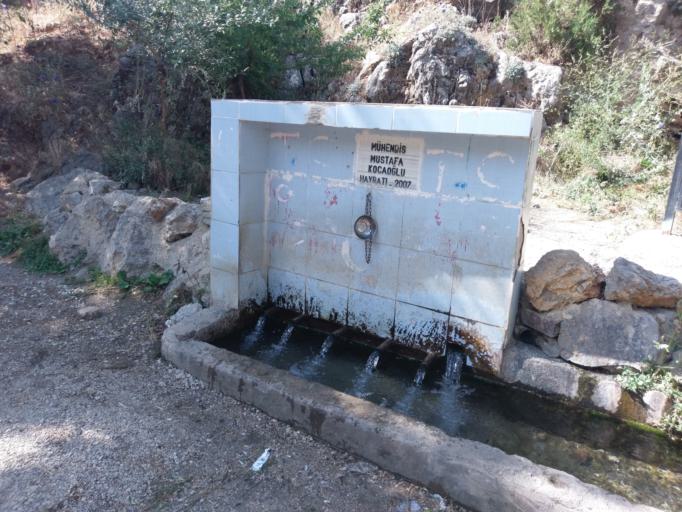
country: TR
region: Adana
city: Tufanbeyli
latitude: 38.3471
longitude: 36.2336
